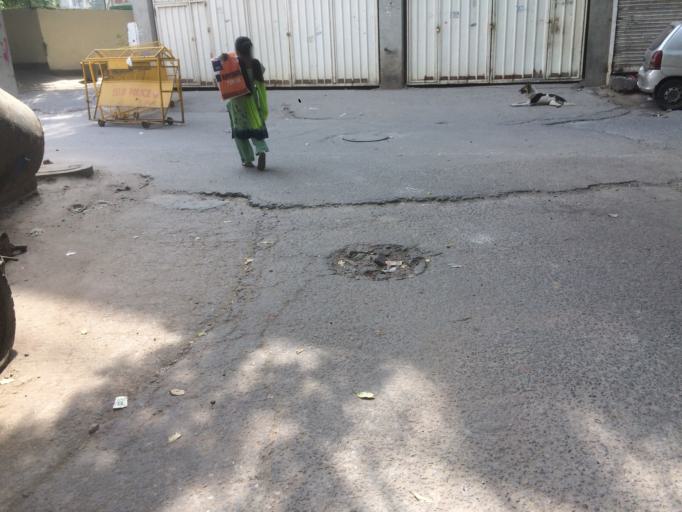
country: IN
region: NCT
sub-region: Central Delhi
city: Karol Bagh
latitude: 28.6232
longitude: 77.1358
